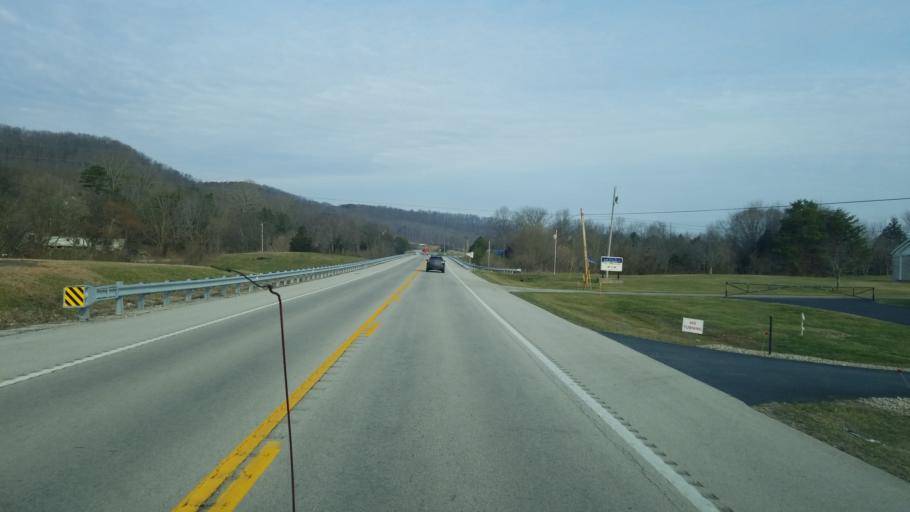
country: US
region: Kentucky
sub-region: Russell County
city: Russell Springs
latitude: 37.1704
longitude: -85.0074
